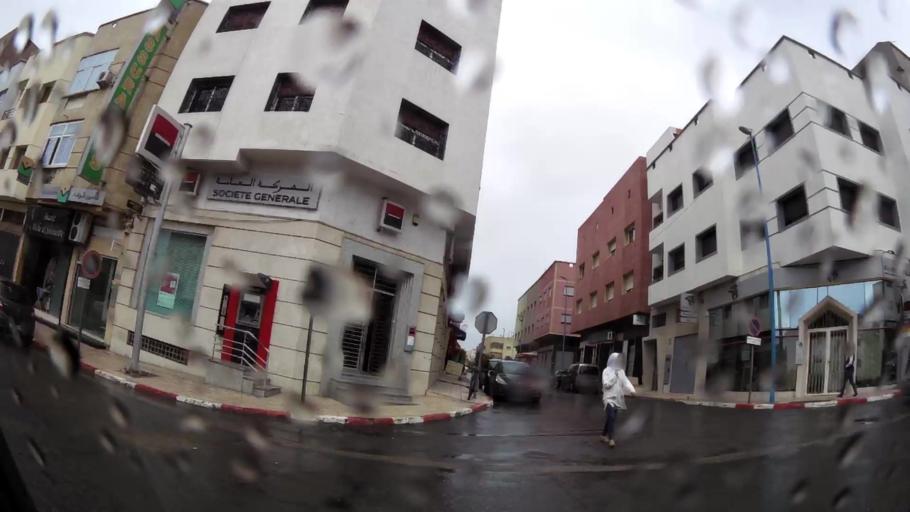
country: MA
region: Grand Casablanca
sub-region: Mediouna
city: Tit Mellil
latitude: 33.6194
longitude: -7.4863
